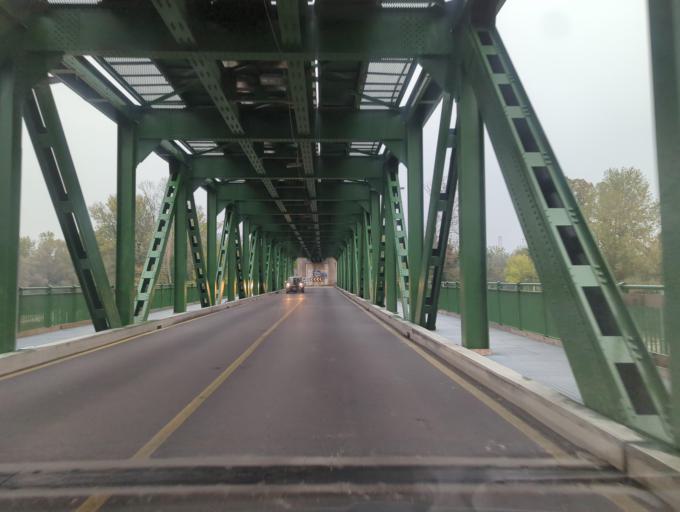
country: IT
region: Lombardy
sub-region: Citta metropolitana di Milano
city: Turbigo
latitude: 45.5085
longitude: 8.7199
